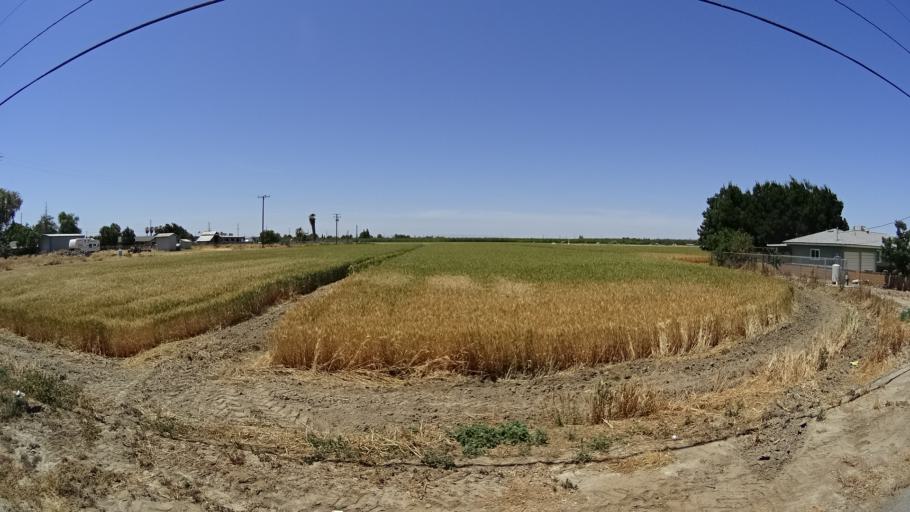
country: US
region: California
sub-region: Kings County
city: Armona
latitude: 36.3155
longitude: -119.7180
